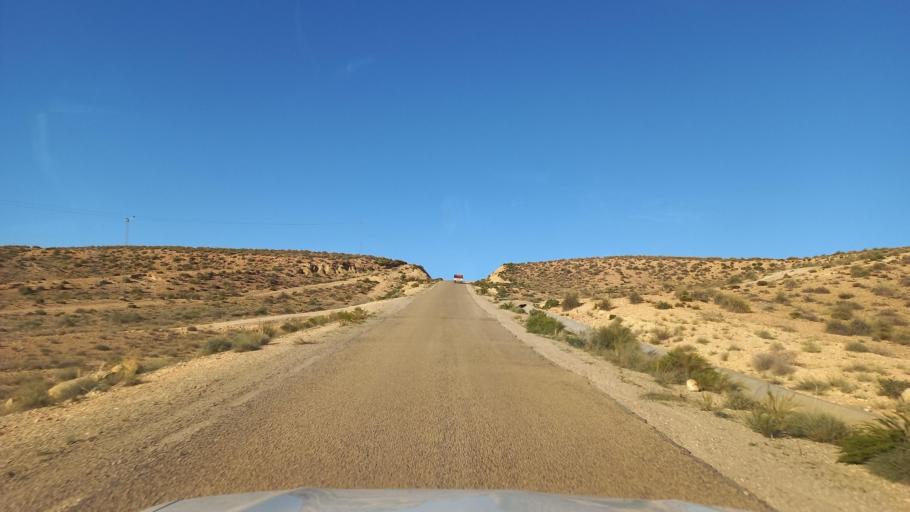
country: TN
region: Al Qasrayn
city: Sbiba
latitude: 35.3478
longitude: 9.1305
